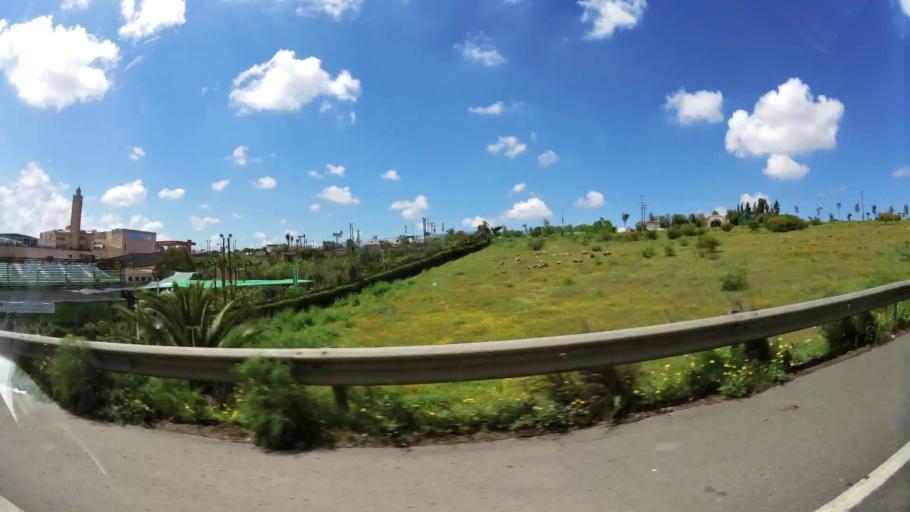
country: MA
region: Grand Casablanca
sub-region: Nouaceur
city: Bouskoura
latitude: 33.4883
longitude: -7.6312
